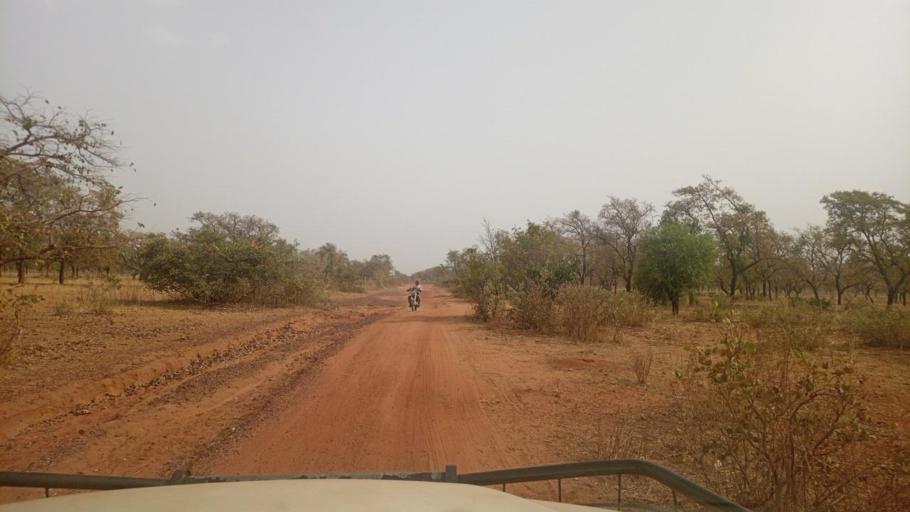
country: BF
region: Boucle du Mouhoun
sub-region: Province des Banwa
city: Salanso
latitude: 12.1066
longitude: -4.3352
